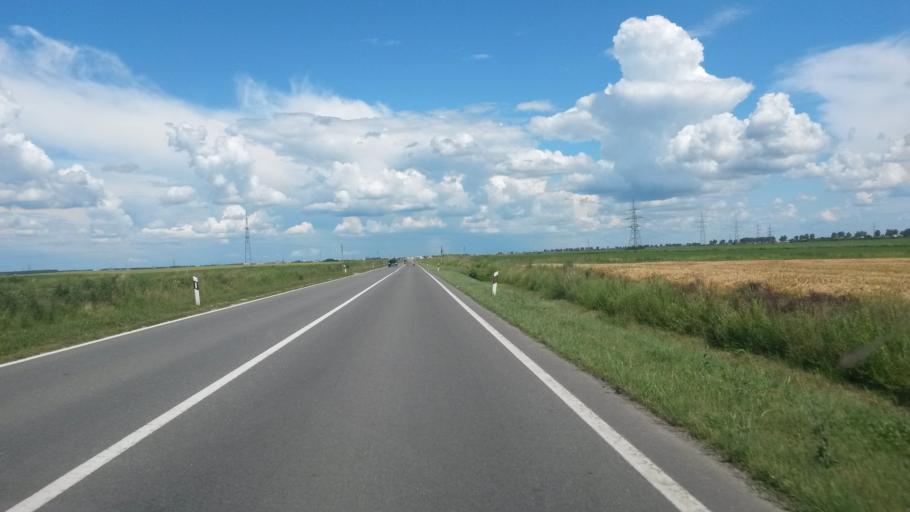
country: HR
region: Osjecko-Baranjska
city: Cepin
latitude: 45.5391
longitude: 18.5763
